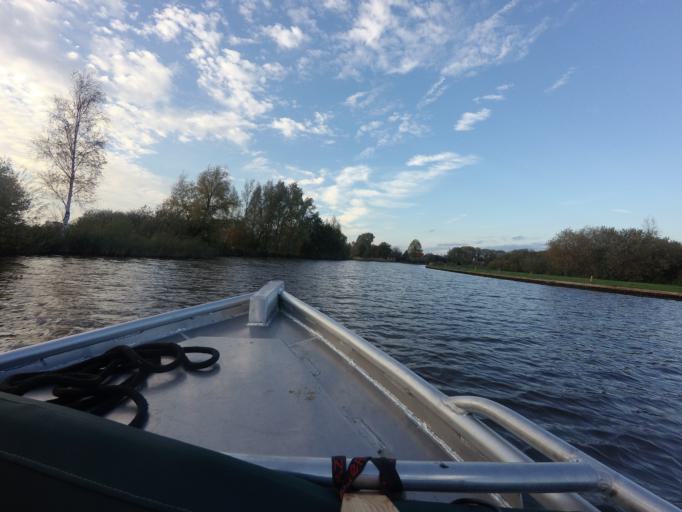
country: NL
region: Overijssel
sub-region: Gemeente Steenwijkerland
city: Blokzijl
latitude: 52.7391
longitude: 5.9938
